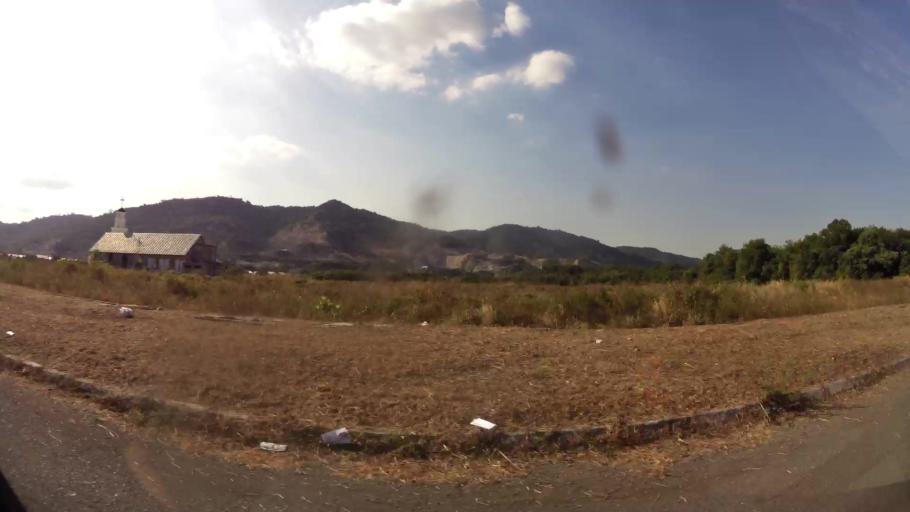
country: EC
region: Guayas
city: Santa Lucia
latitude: -2.1916
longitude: -79.9993
